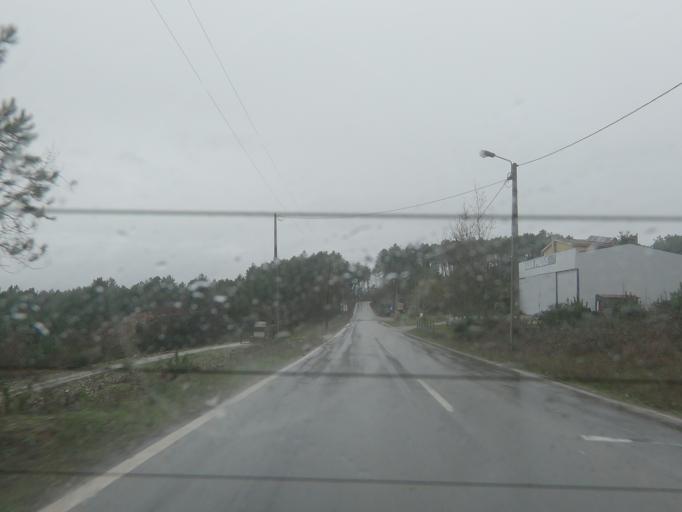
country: PT
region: Vila Real
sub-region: Sabrosa
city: Vilela
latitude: 41.2253
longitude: -7.6773
